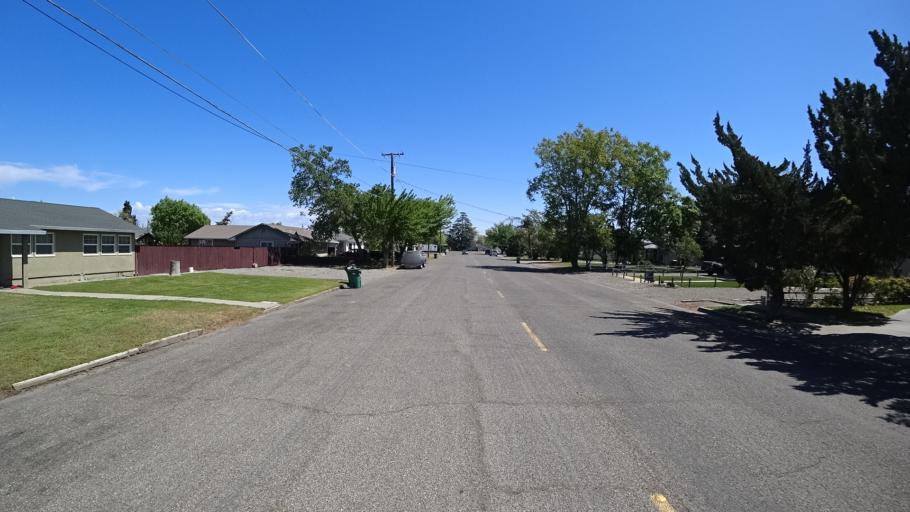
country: US
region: California
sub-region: Glenn County
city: Orland
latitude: 39.7451
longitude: -122.1843
